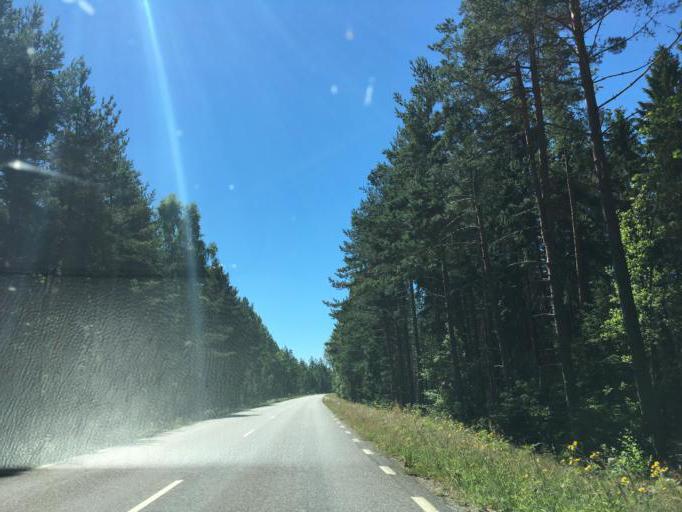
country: SE
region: OErebro
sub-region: Laxa Kommun
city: Laxa
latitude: 58.8512
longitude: 14.5482
